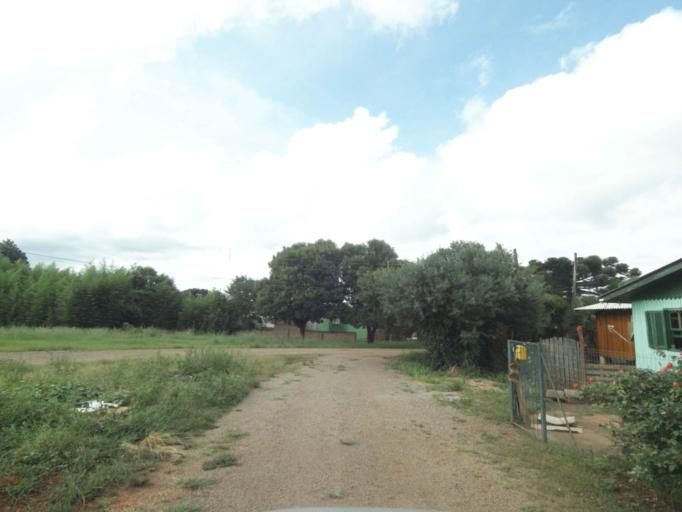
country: BR
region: Rio Grande do Sul
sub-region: Lagoa Vermelha
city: Lagoa Vermelha
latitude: -28.2104
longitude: -51.5337
